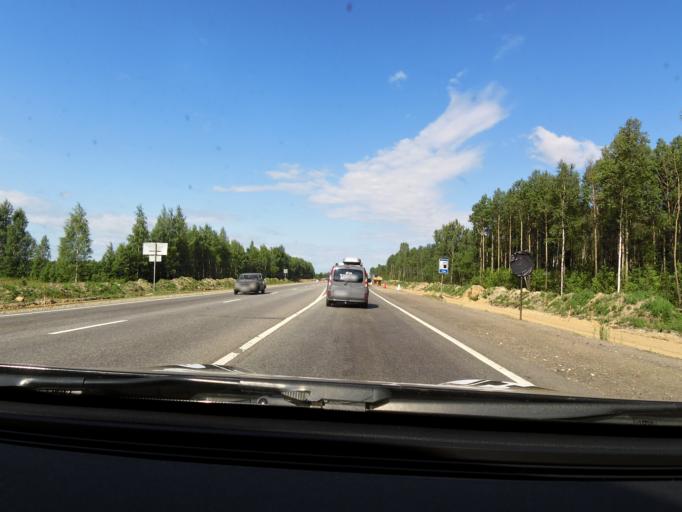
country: RU
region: Tverskaya
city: Emmaus
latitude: 56.7830
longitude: 35.9974
